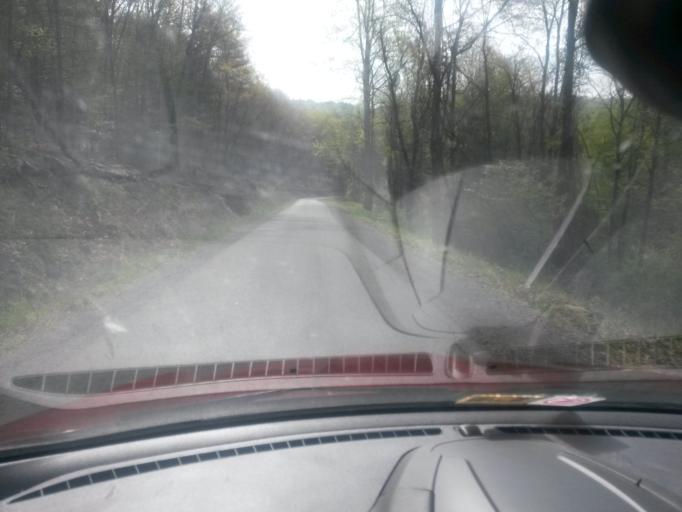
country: US
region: West Virginia
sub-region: Pocahontas County
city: Marlinton
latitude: 38.0888
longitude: -80.2230
